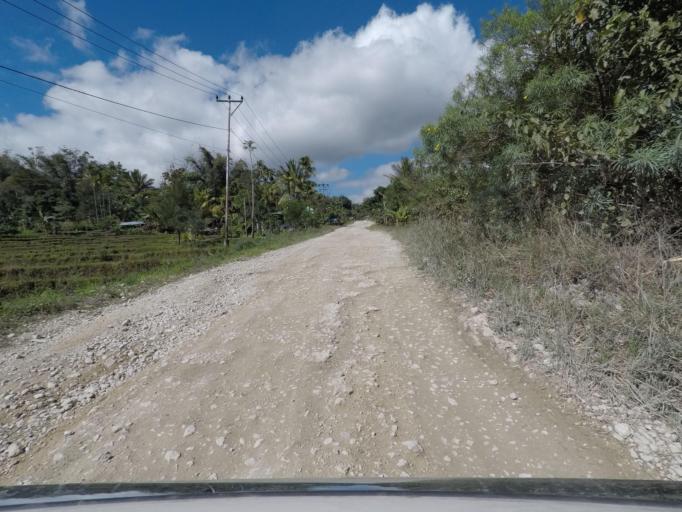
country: TL
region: Baucau
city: Venilale
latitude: -8.6702
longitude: 126.3666
